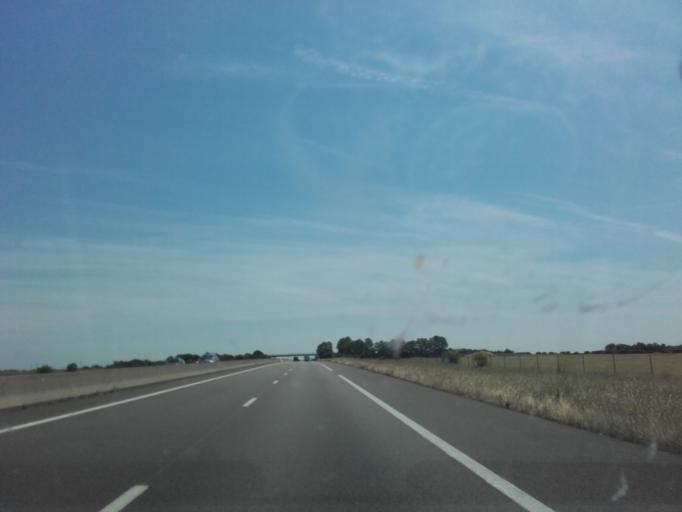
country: FR
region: Bourgogne
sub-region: Departement de la Cote-d'Or
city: Semur-en-Auxois
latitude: 47.4888
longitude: 4.1425
